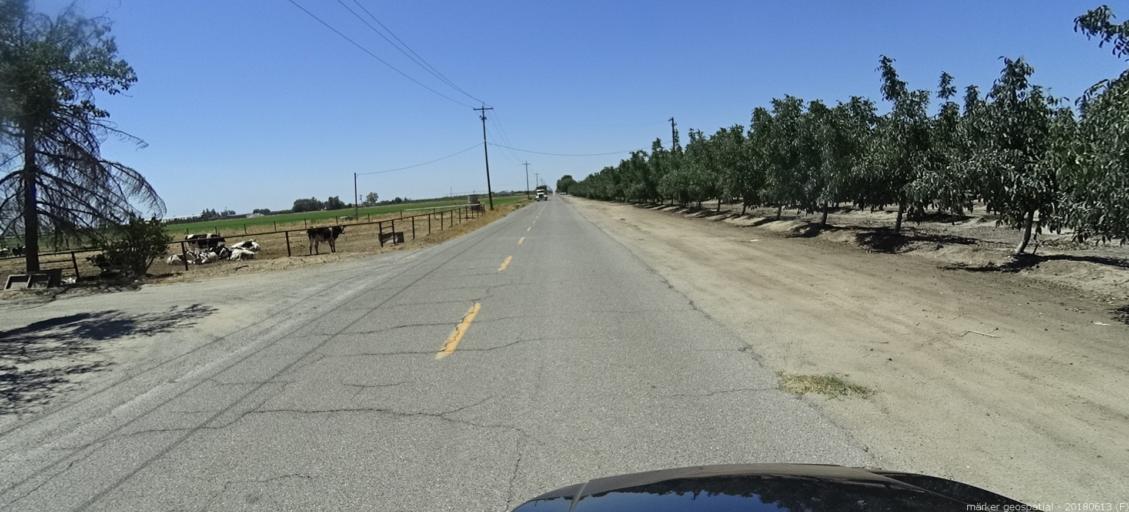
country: US
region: California
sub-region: Madera County
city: Chowchilla
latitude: 37.0433
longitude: -120.3106
